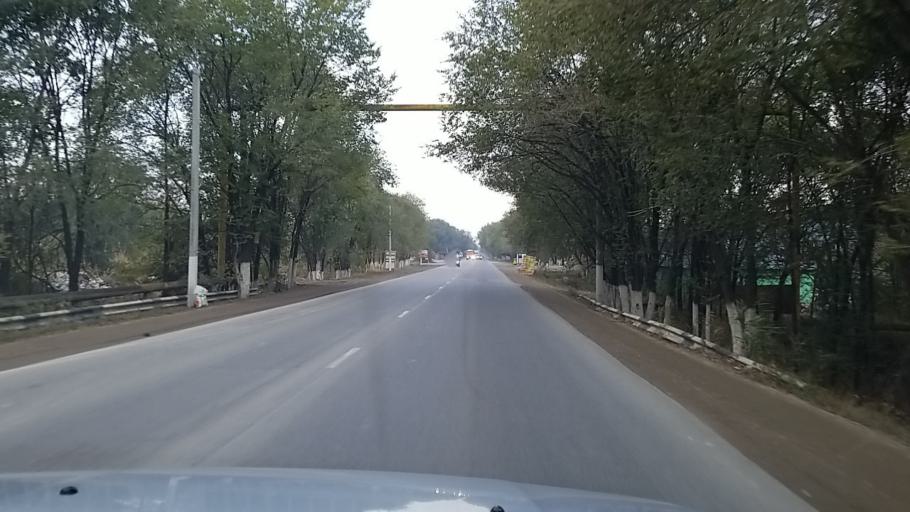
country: KZ
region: Almaty Oblysy
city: Burunday
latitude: 43.3554
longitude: 76.8040
